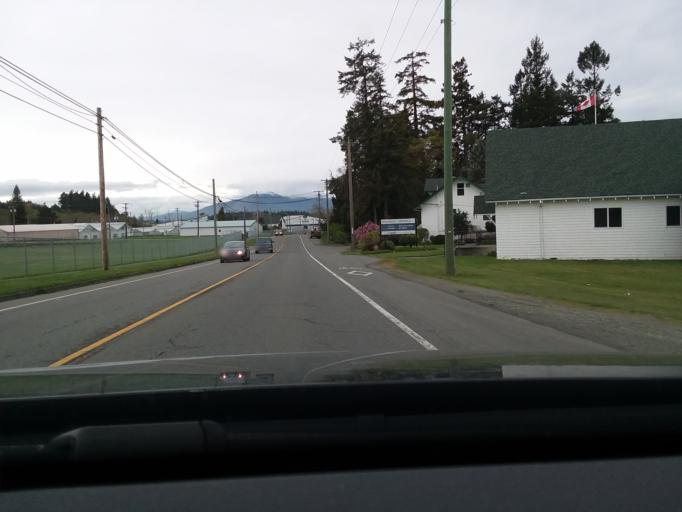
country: CA
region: British Columbia
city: North Saanich
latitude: 48.6203
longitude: -123.4171
